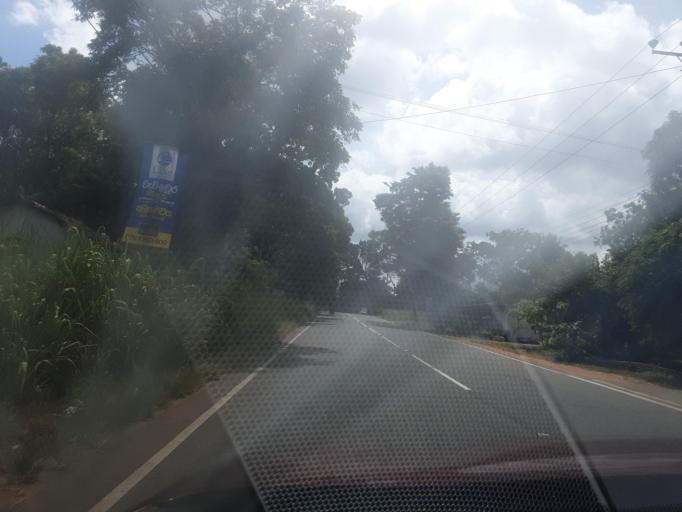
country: LK
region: North Western
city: Kuliyapitiya
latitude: 7.4809
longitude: 79.9955
